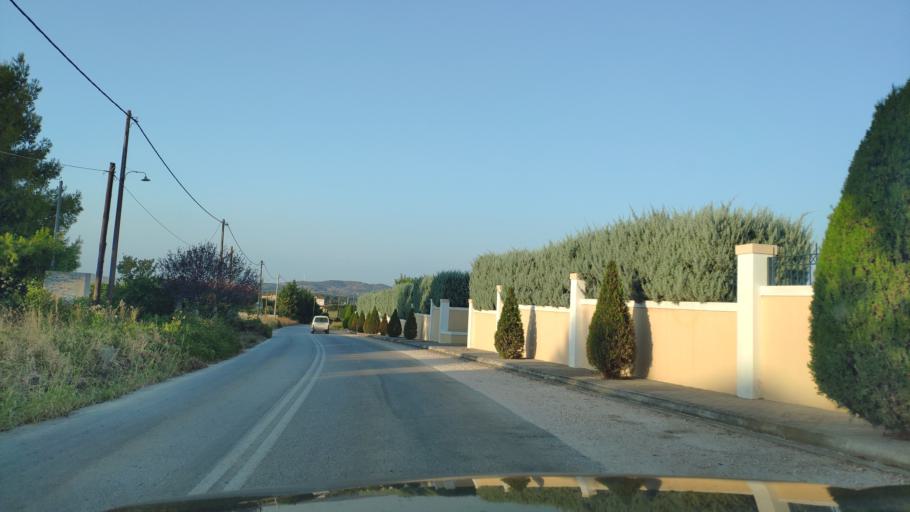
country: GR
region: Attica
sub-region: Nomarchia Anatolikis Attikis
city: Markopoulo
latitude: 37.9010
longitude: 23.9583
